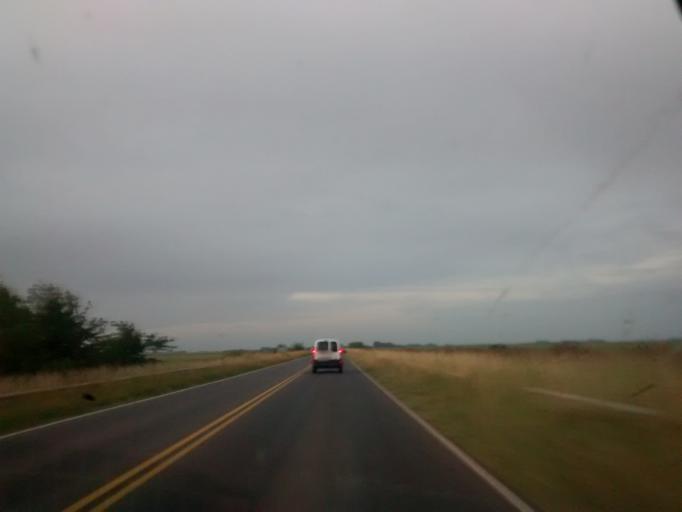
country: AR
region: Buenos Aires
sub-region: Partido de General Belgrano
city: General Belgrano
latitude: -35.7011
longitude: -58.4800
